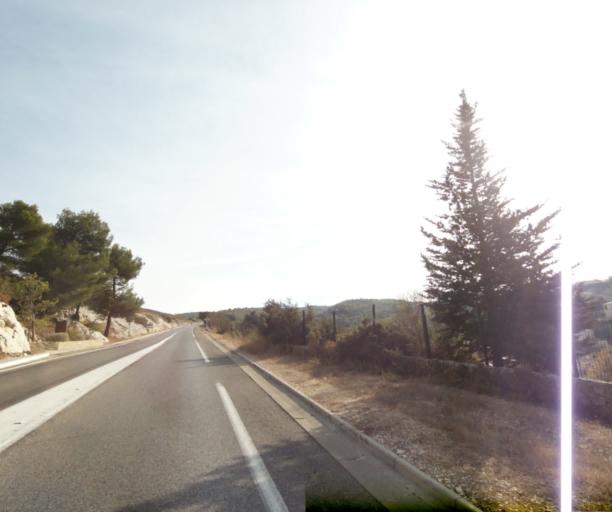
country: FR
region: Provence-Alpes-Cote d'Azur
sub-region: Departement des Bouches-du-Rhone
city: Ensues-la-Redonne
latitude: 43.3574
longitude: 5.2093
